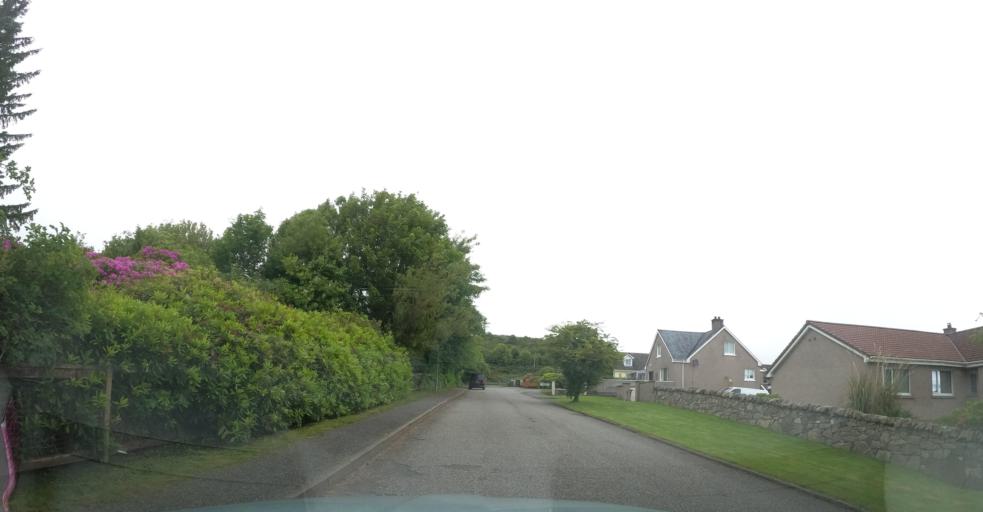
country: GB
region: Scotland
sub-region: Eilean Siar
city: Isle of Lewis
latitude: 58.2200
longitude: -6.3990
